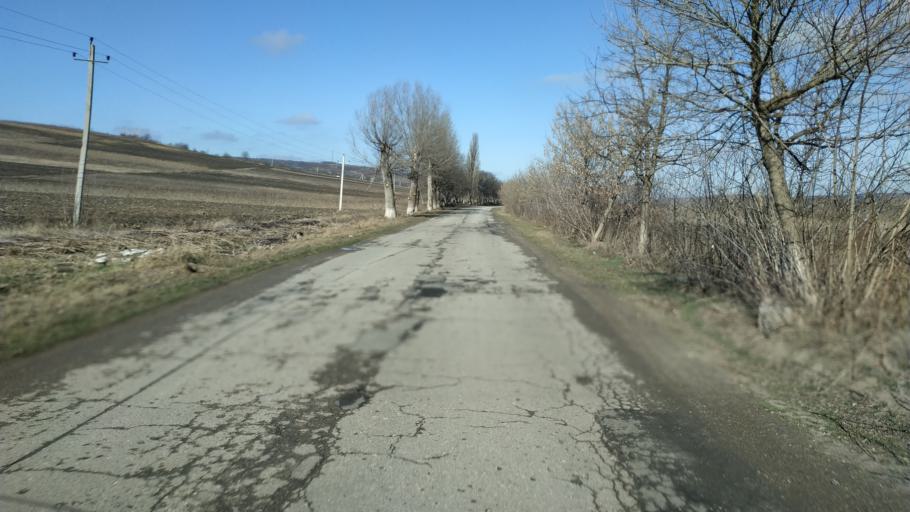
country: MD
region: Hincesti
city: Hincesti
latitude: 46.9470
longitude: 28.6189
